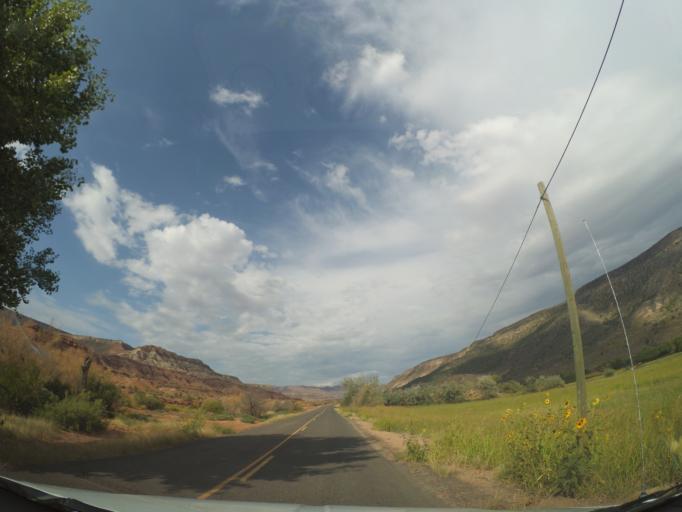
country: US
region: Utah
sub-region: Washington County
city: LaVerkin
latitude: 37.2156
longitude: -113.1683
